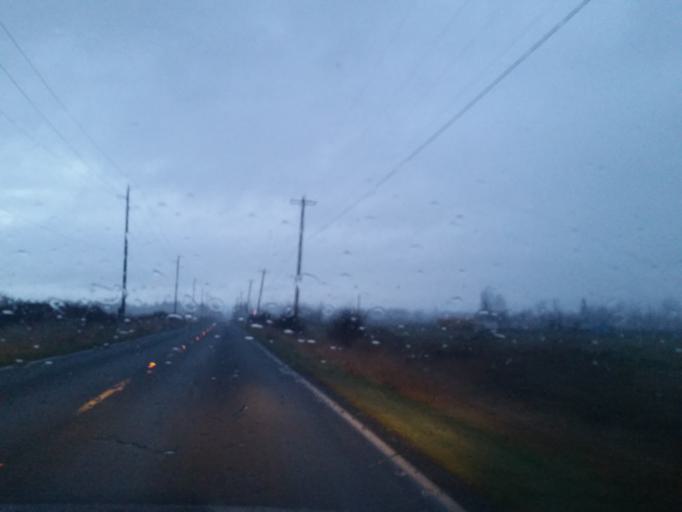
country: US
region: Washington
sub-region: Snohomish County
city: Everett
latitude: 47.9566
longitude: -122.1738
